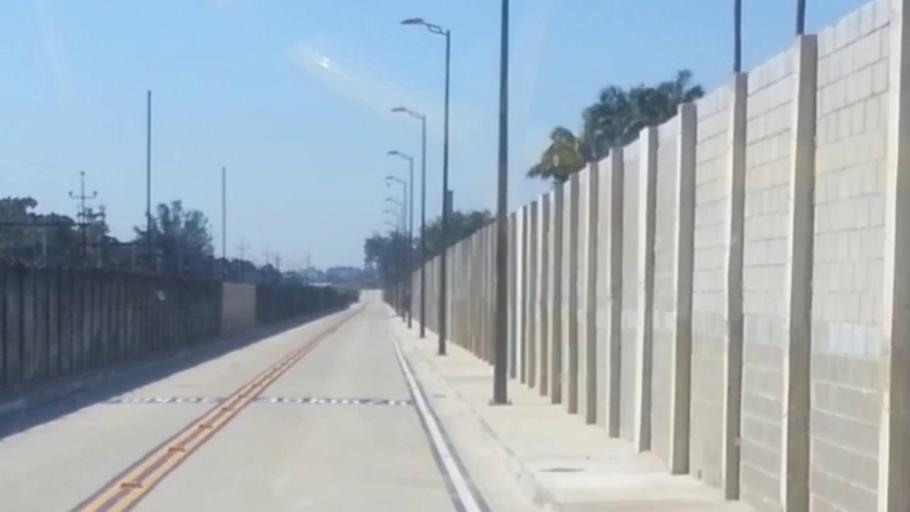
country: BR
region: Rio de Janeiro
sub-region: Nilopolis
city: Nilopolis
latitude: -22.8636
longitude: -43.4034
